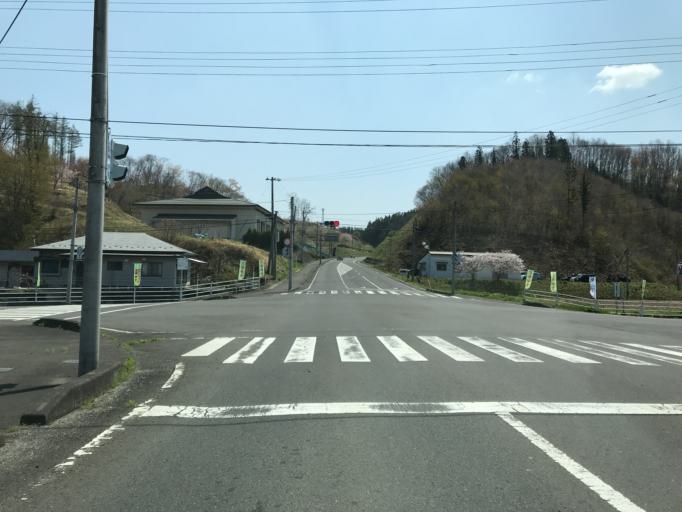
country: JP
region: Fukushima
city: Ishikawa
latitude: 37.0441
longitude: 140.5034
